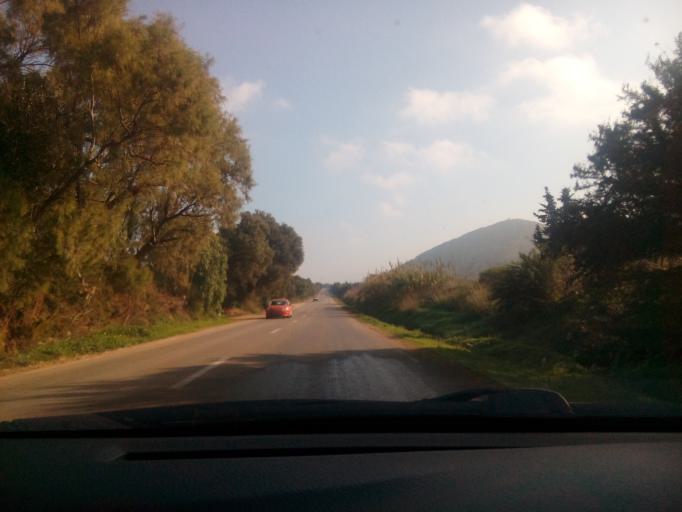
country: DZ
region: Oran
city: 'Ain el Turk
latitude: 35.7030
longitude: -0.8495
